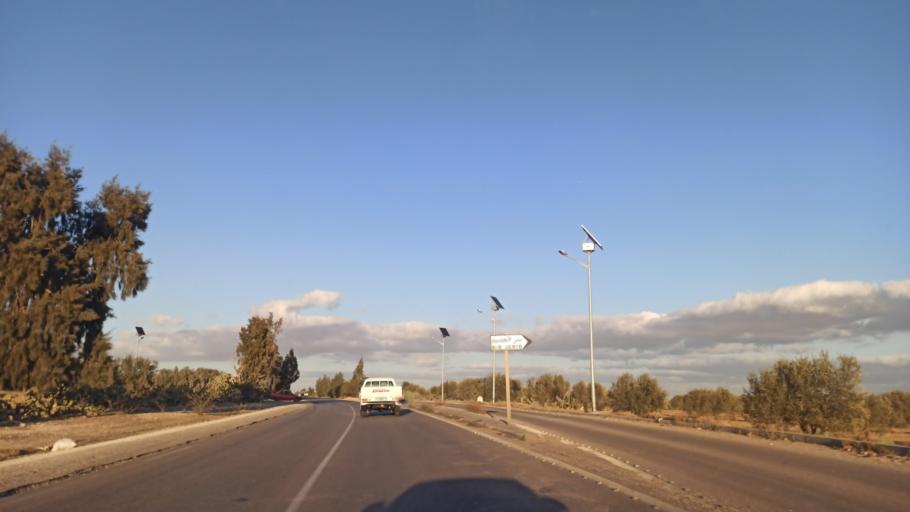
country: TN
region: Al Qayrawan
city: Sbikha
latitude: 35.8548
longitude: 10.2000
